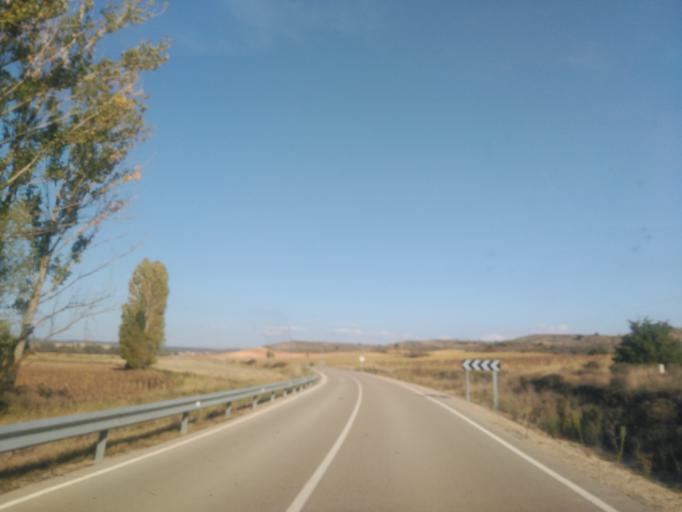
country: ES
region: Castille and Leon
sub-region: Provincia de Soria
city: Alcubilla de Avellaneda
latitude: 41.7548
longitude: -3.2571
